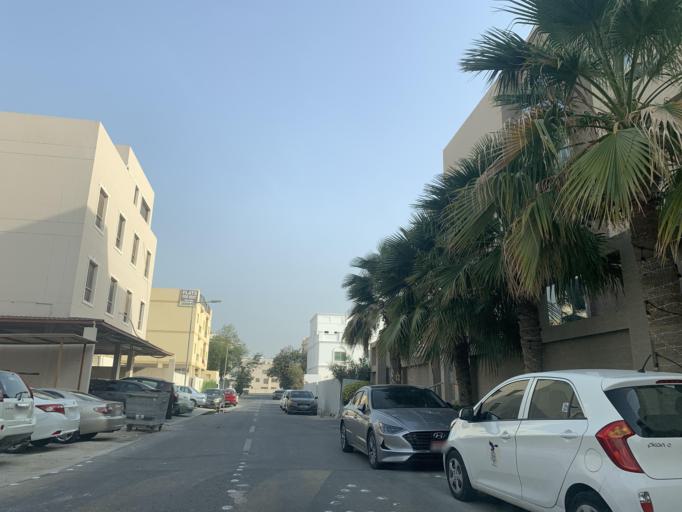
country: BH
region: Northern
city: Madinat `Isa
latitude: 26.1918
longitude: 50.5651
